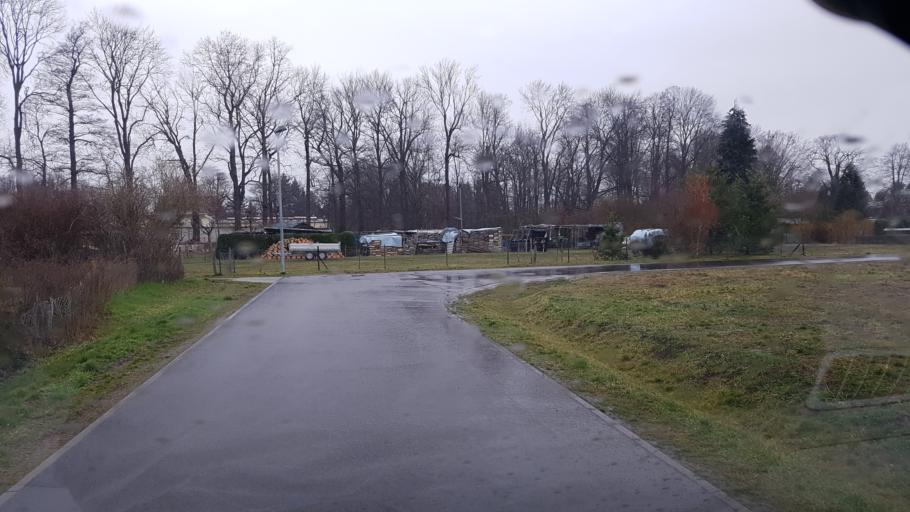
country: DE
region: Brandenburg
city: Ruhland
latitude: 51.4549
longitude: 13.8588
